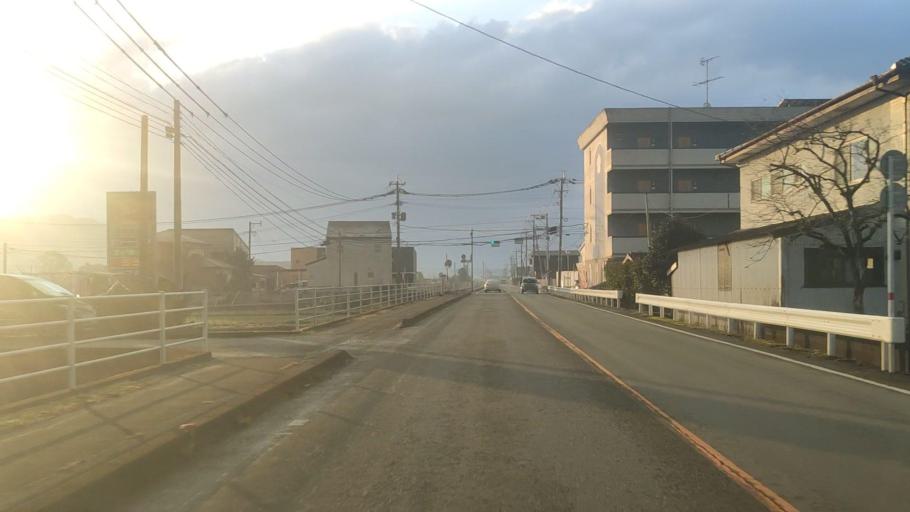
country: JP
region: Kumamoto
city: Uto
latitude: 32.7131
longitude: 130.7741
